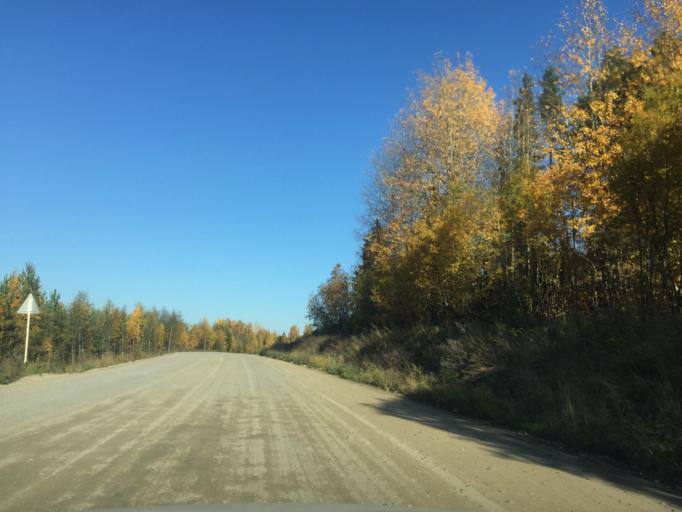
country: RU
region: Leningrad
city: Kuznechnoye
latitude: 61.3171
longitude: 29.9443
